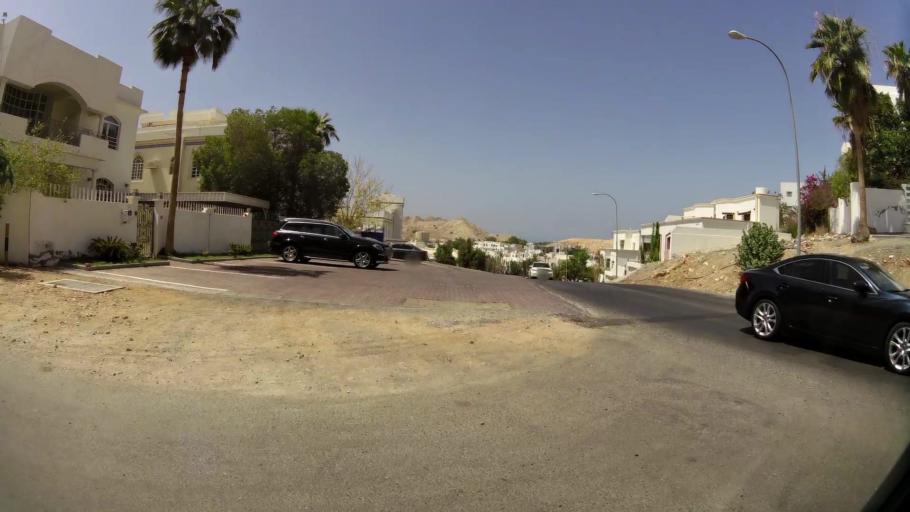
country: OM
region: Muhafazat Masqat
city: Muscat
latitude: 23.6177
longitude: 58.5035
